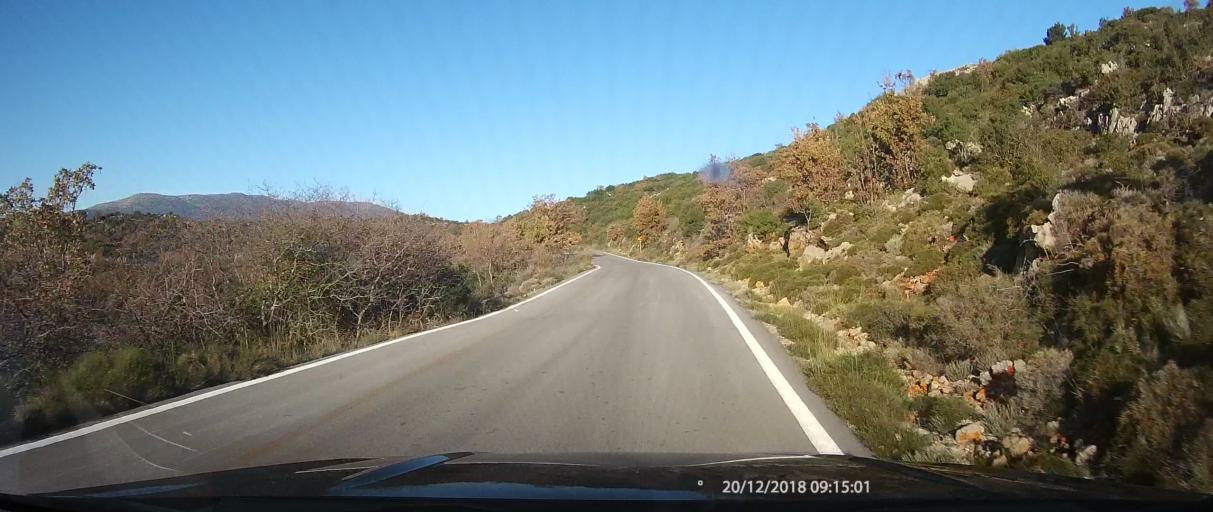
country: GR
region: Peloponnese
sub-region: Nomos Lakonias
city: Sykea
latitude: 36.9027
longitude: 22.9818
